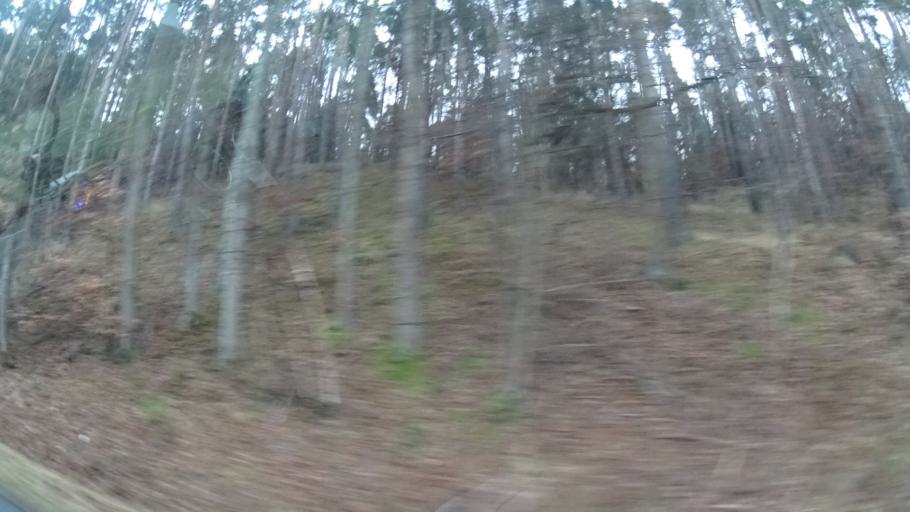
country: DE
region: Thuringia
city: Rausdorf
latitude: 50.8631
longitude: 11.6934
